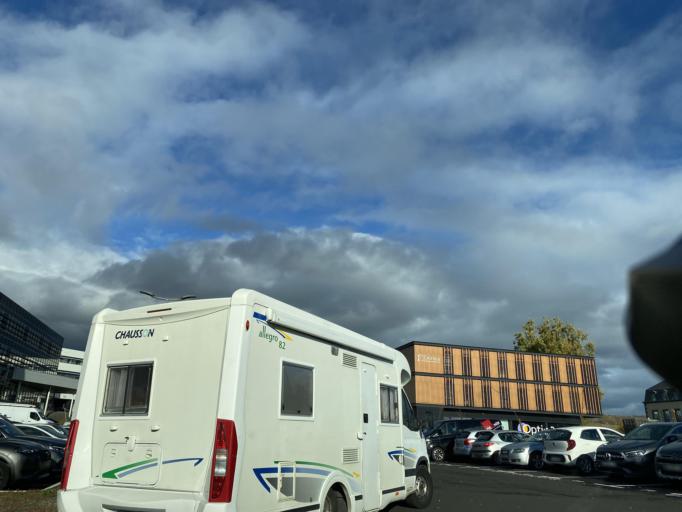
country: FR
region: Auvergne
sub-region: Departement du Puy-de-Dome
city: Perignat-les-Sarlieve
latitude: 45.7398
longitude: 3.1601
